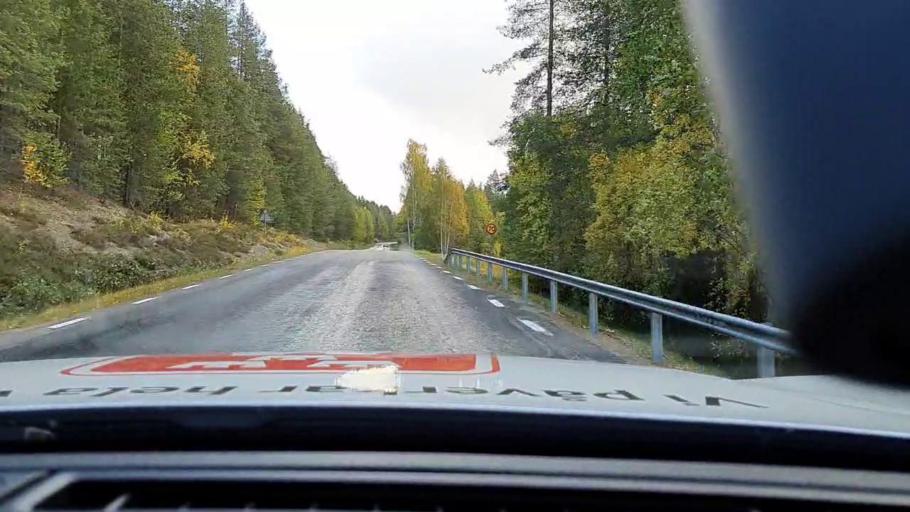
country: SE
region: Vaesterbotten
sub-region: Skelleftea Kommun
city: Langsele
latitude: 64.9621
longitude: 19.8918
